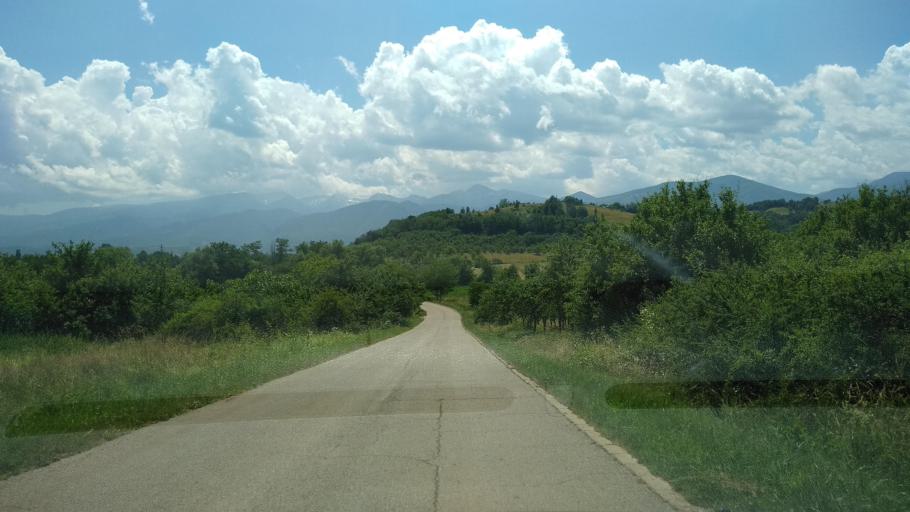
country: RO
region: Hunedoara
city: Densus
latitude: 45.5596
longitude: 22.8187
